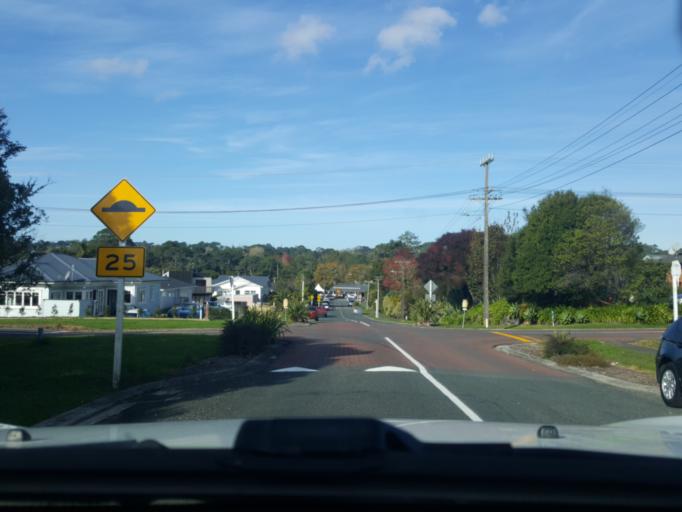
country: NZ
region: Auckland
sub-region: Auckland
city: Rosebank
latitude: -36.7586
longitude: 174.5948
